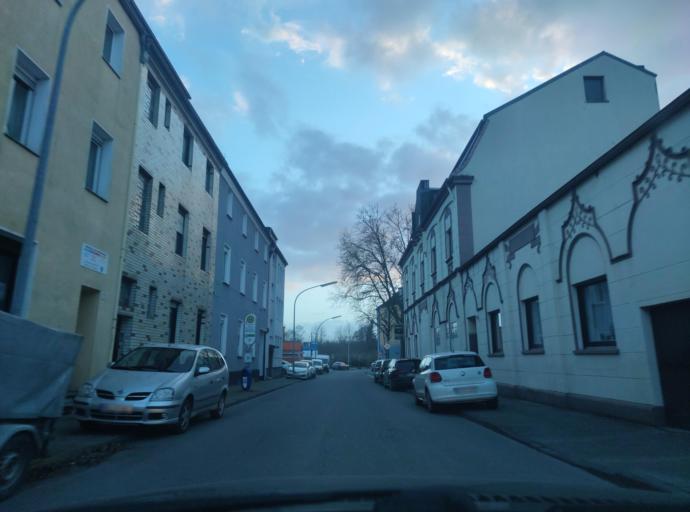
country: DE
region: North Rhine-Westphalia
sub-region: Regierungsbezirk Munster
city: Gelsenkirchen
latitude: 51.4888
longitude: 7.0901
